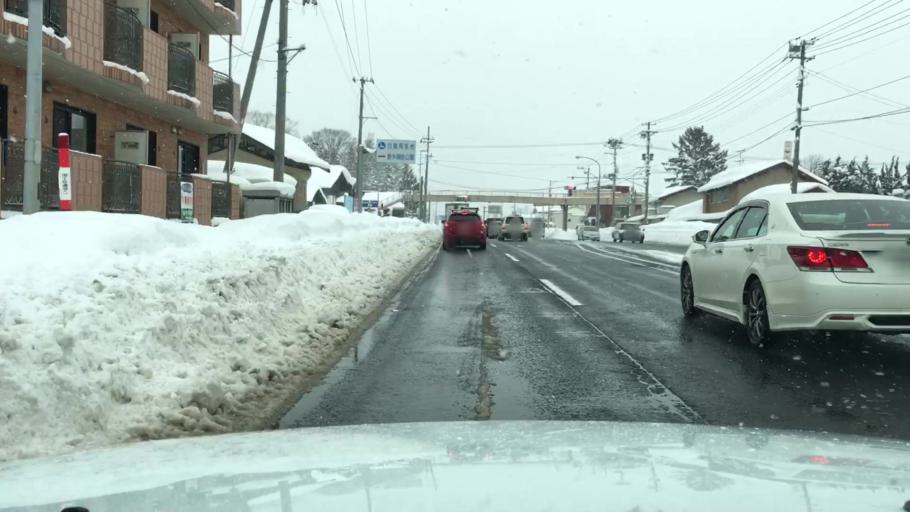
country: JP
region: Aomori
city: Hirosaki
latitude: 40.6461
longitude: 140.4989
